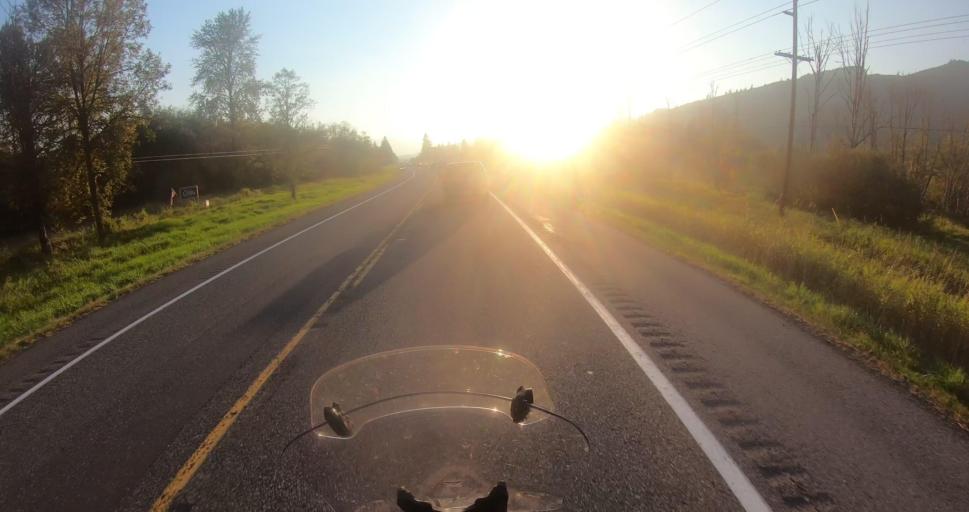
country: US
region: Washington
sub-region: Lewis County
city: Morton
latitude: 46.5373
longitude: -122.1143
